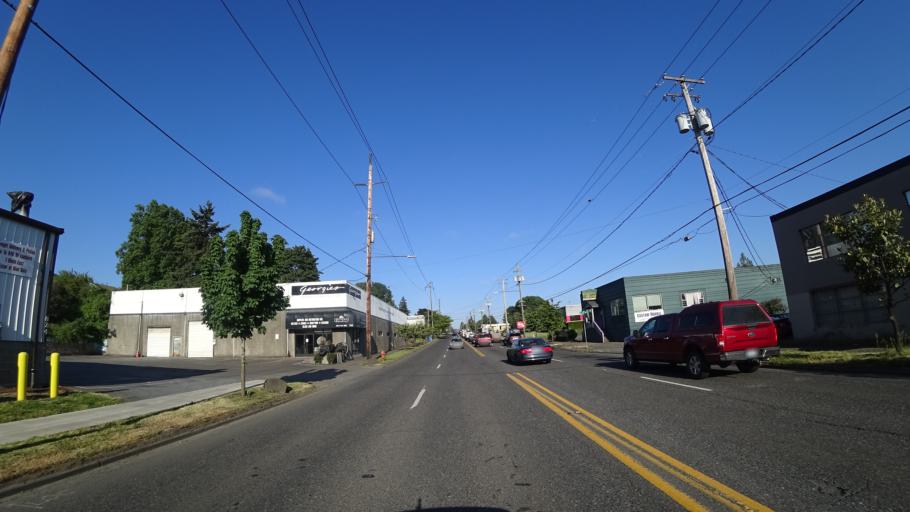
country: US
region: Oregon
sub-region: Multnomah County
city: Portland
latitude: 45.5772
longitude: -122.6565
